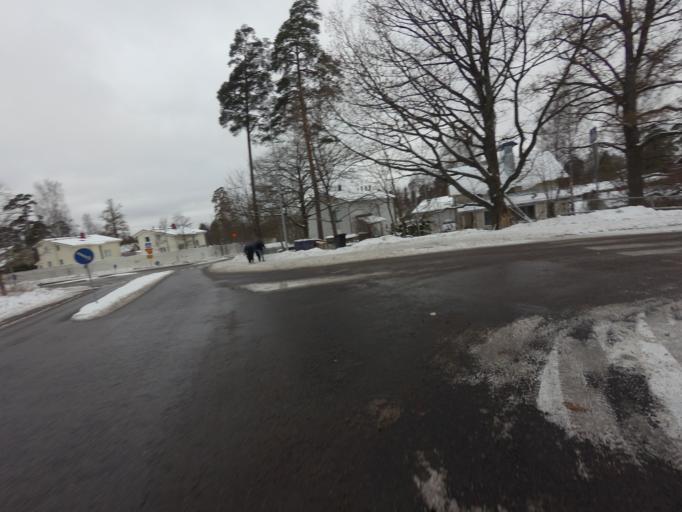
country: FI
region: Uusimaa
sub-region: Helsinki
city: Vantaa
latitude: 60.1839
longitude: 25.0509
